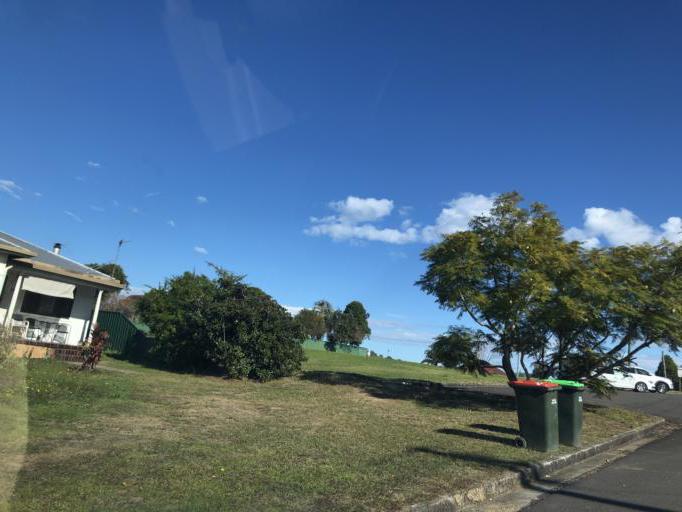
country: AU
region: New South Wales
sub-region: Nambucca Shire
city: Bowraville
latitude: -30.6490
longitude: 152.8533
